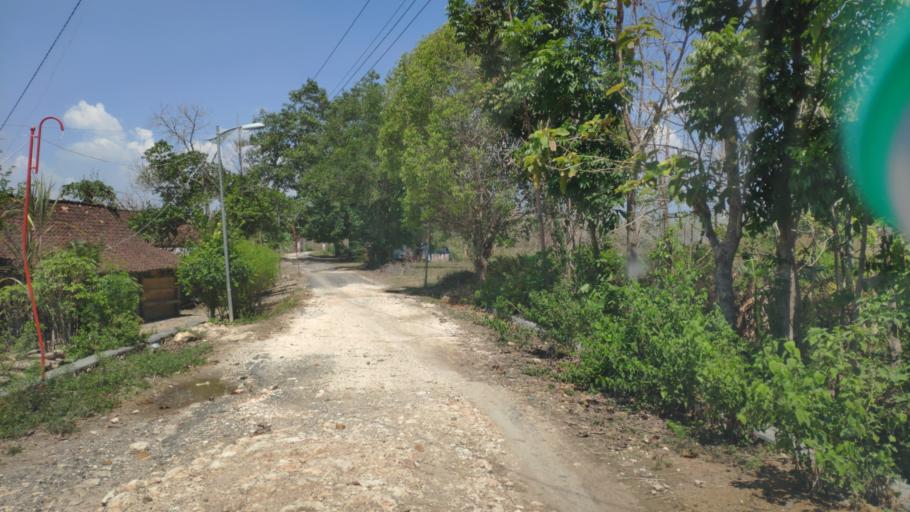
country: ID
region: Central Java
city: Galuk
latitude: -7.1085
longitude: 111.4901
